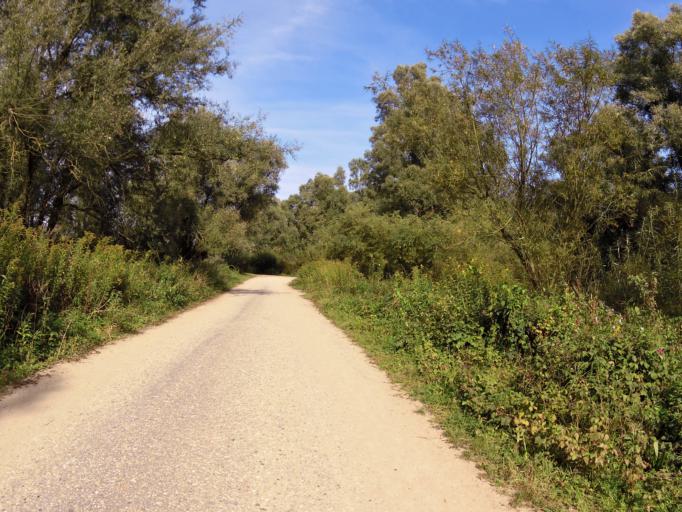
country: NL
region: Gelderland
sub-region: Gemeente Duiven
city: Duiven
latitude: 51.8657
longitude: 5.9999
